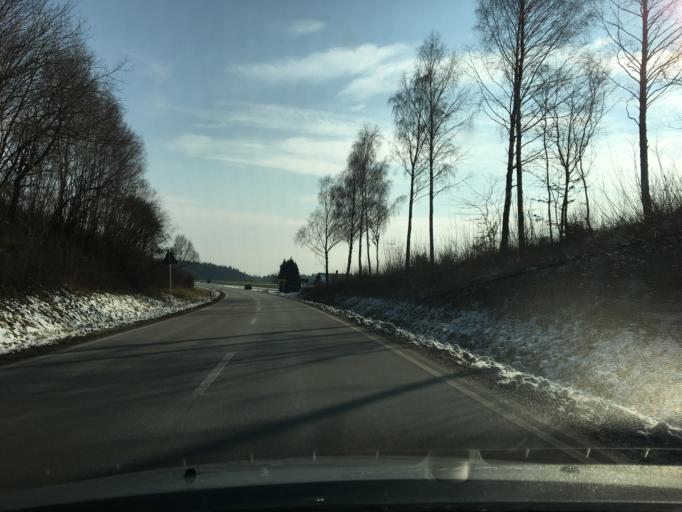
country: DE
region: Bavaria
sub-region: Lower Bavaria
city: Gangkofen
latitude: 48.4109
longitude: 12.5447
